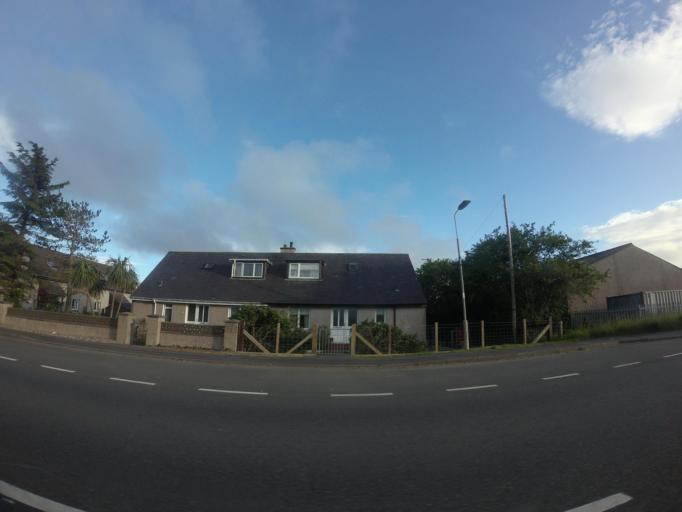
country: GB
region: Scotland
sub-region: Eilean Siar
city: Stornoway
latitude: 58.2029
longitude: -6.3412
